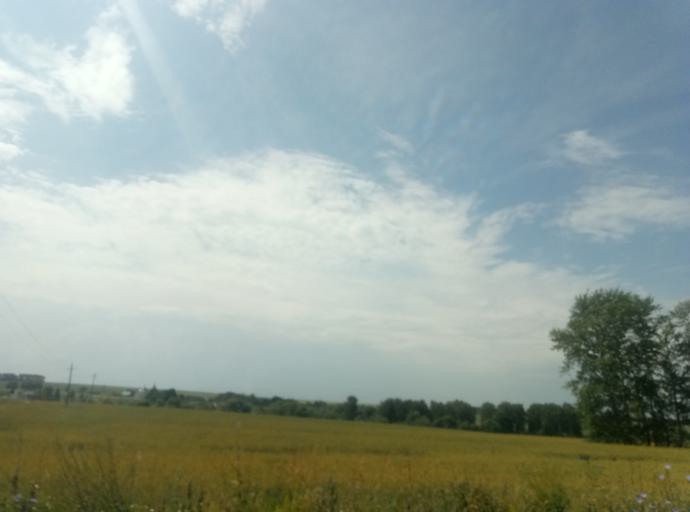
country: RU
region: Tula
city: Kireyevsk
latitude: 53.8985
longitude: 37.9857
